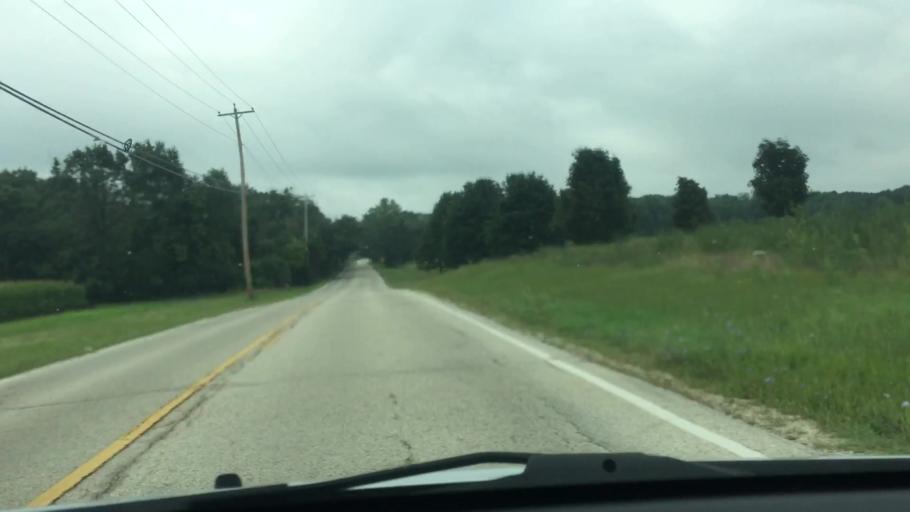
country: US
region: Wisconsin
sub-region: Waukesha County
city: Dousman
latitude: 43.0439
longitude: -88.4425
